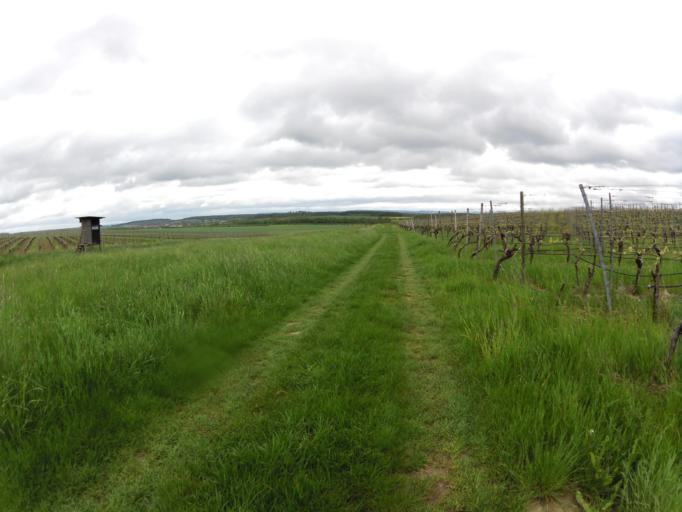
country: DE
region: Bavaria
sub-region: Regierungsbezirk Unterfranken
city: Sommerach
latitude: 49.8407
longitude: 10.2158
